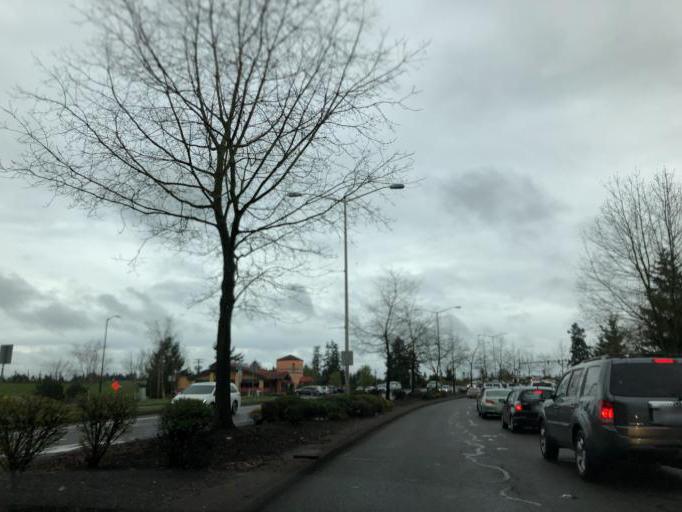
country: US
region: Washington
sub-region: Thurston County
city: Tanglewilde-Thompson Place
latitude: 47.0663
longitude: -122.7670
